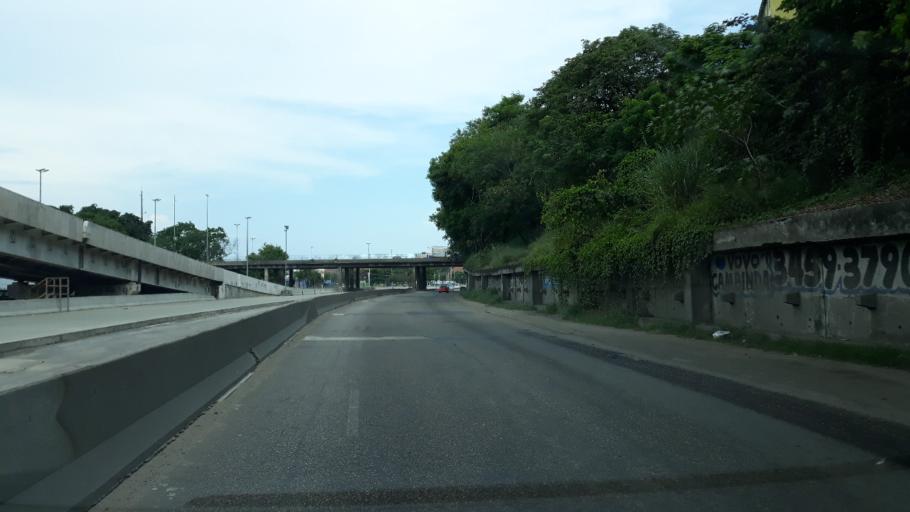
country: BR
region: Rio de Janeiro
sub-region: Duque De Caxias
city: Duque de Caxias
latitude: -22.8156
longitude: -43.2904
